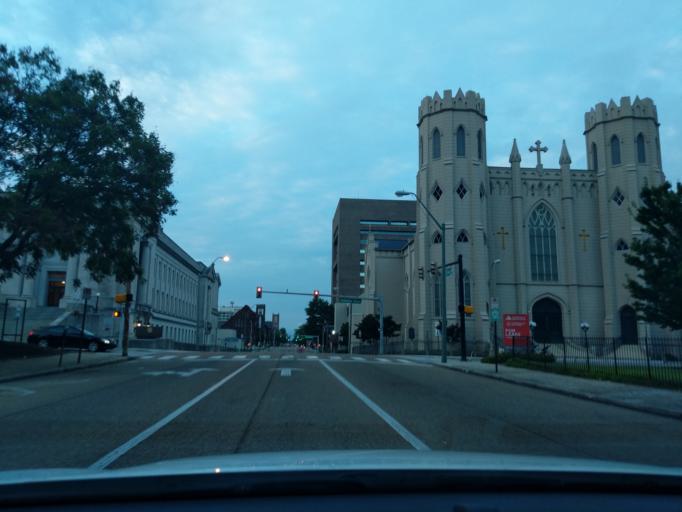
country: US
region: Tennessee
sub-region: Shelby County
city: Memphis
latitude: 35.1474
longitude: -90.0492
